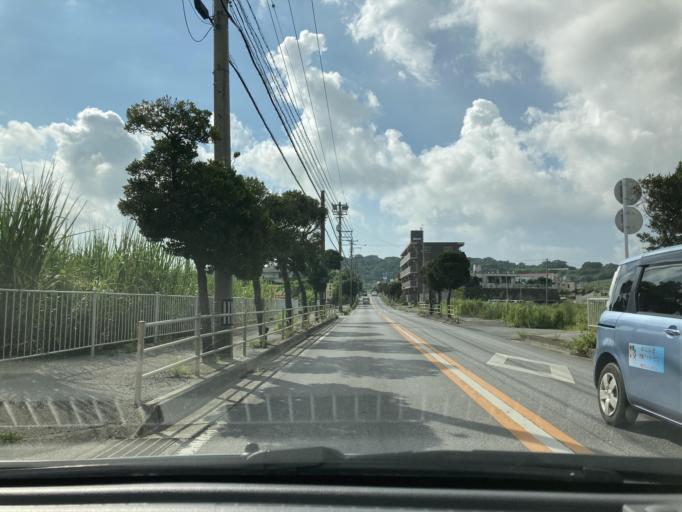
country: JP
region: Okinawa
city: Tomigusuku
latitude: 26.1557
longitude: 127.7495
